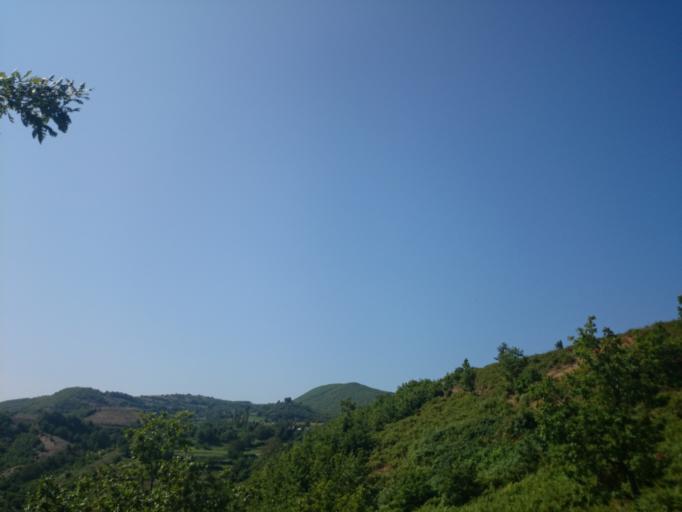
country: AL
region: Diber
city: Peshkopi
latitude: 41.6367
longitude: 20.4089
